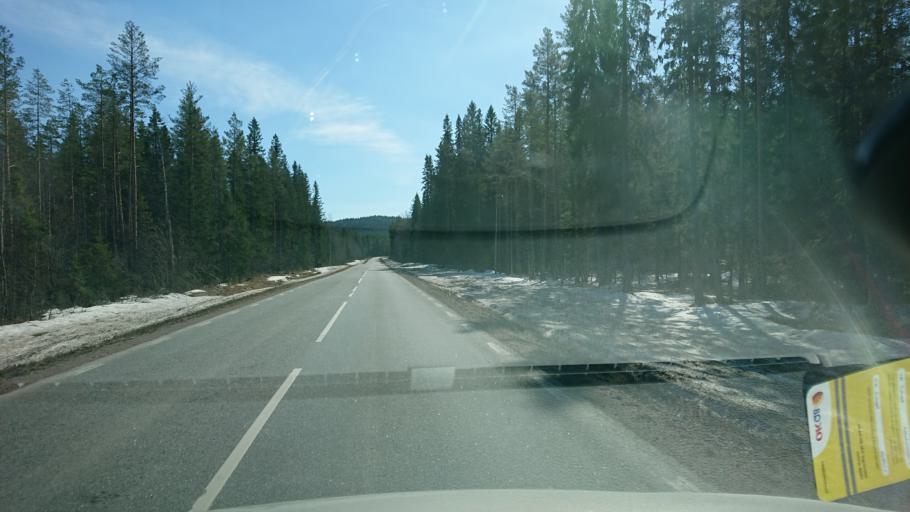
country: SE
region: Vaesternorrland
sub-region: Solleftea Kommun
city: As
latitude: 63.5728
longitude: 16.4461
